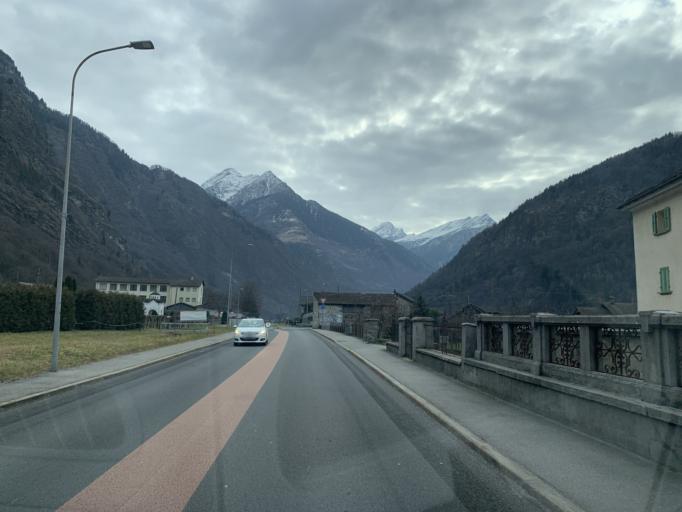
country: CH
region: Ticino
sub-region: Blenio District
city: Acquarossa
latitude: 46.4372
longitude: 8.9558
